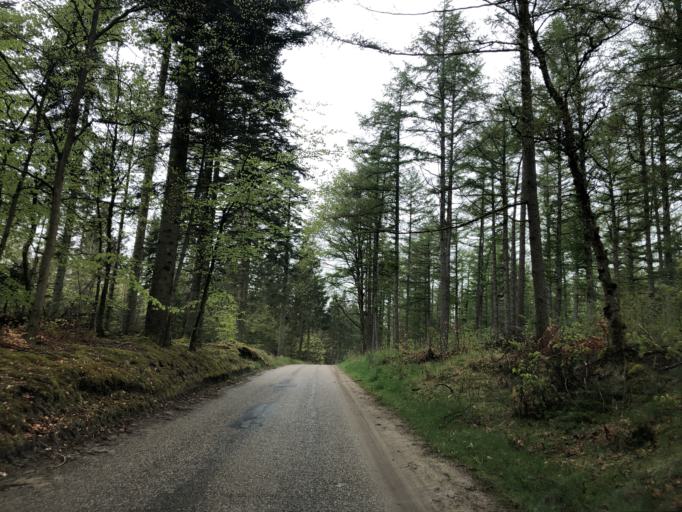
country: DK
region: Central Jutland
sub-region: Lemvig Kommune
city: Lemvig
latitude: 56.4864
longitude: 8.3582
